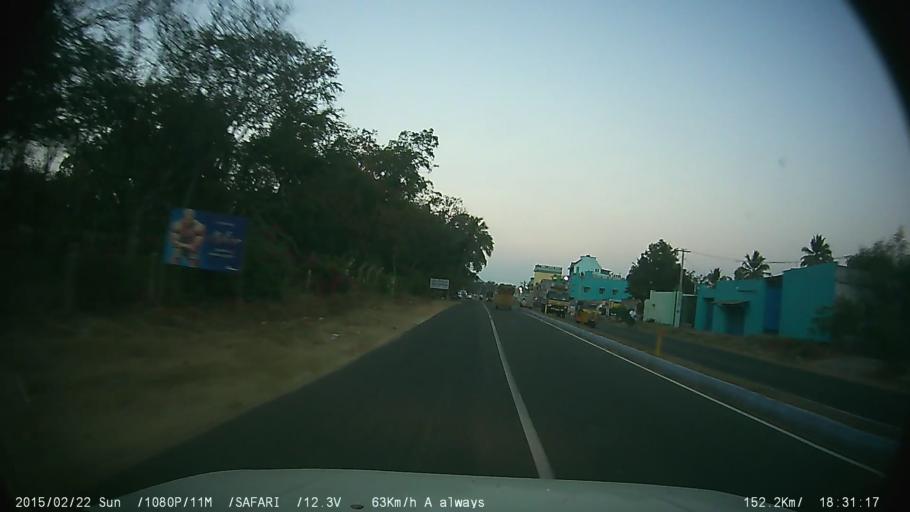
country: IN
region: Tamil Nadu
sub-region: Theni
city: Teni
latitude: 9.9933
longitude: 77.4610
